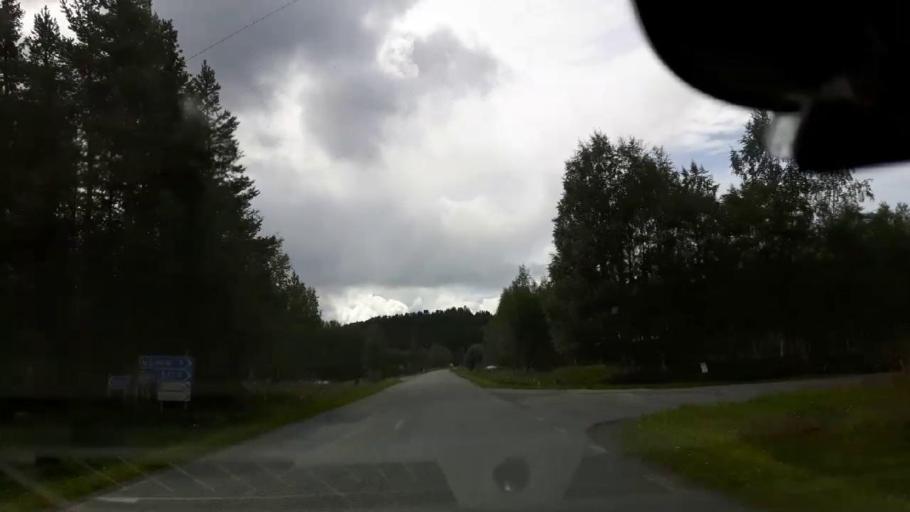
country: SE
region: Jaemtland
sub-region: Krokoms Kommun
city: Valla
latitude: 63.4901
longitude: 13.8857
